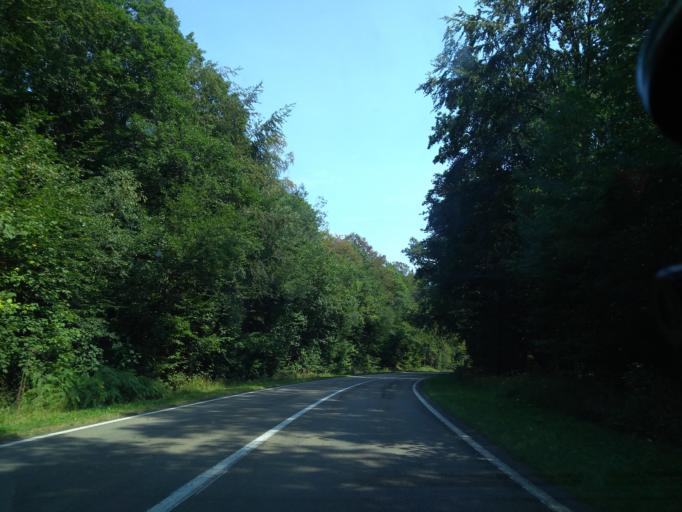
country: BE
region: Wallonia
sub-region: Province du Luxembourg
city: Tenneville
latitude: 50.1334
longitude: 5.4895
